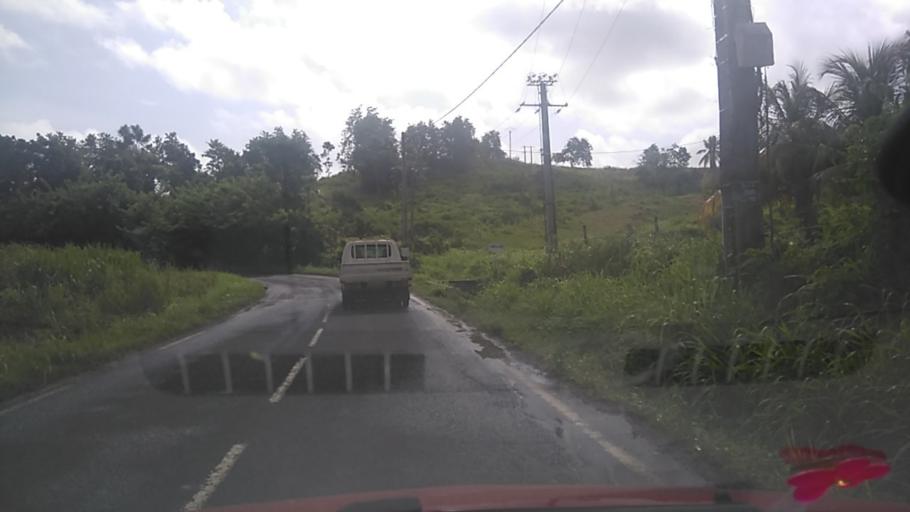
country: MQ
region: Martinique
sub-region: Martinique
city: Saint-Esprit
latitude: 14.5732
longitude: -60.9319
